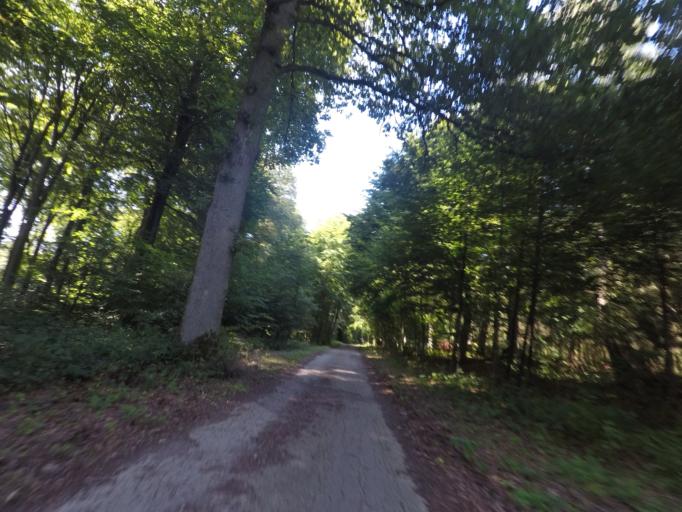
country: LU
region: Luxembourg
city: Bridel
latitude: 49.6464
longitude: 6.0814
